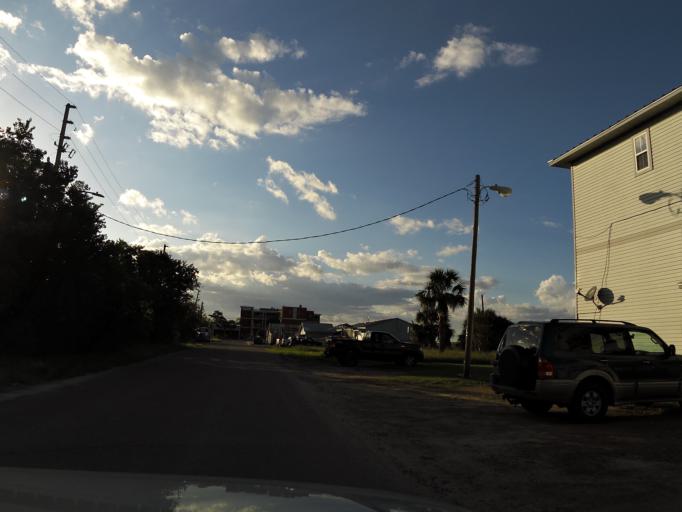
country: US
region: Florida
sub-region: Franklin County
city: Apalachicola
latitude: 29.7306
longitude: -84.9864
